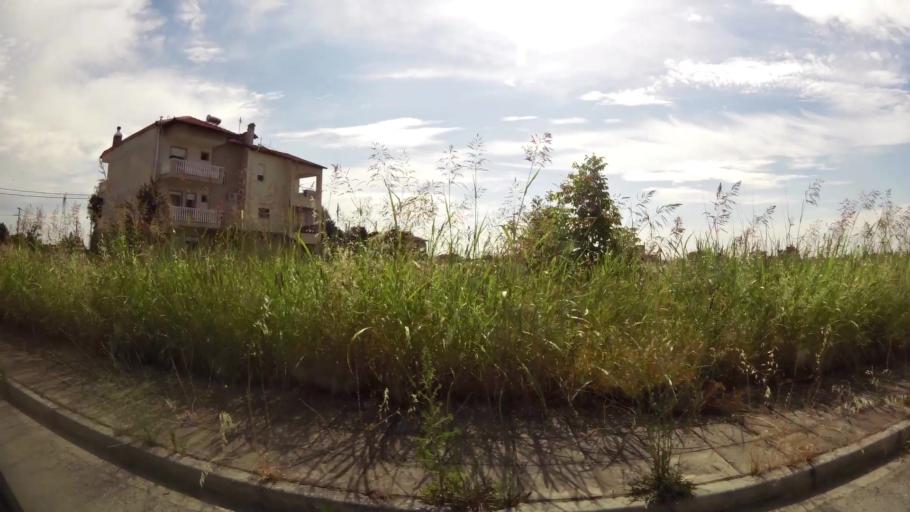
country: GR
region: Central Macedonia
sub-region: Nomos Pierias
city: Katerini
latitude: 40.2858
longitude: 22.5098
